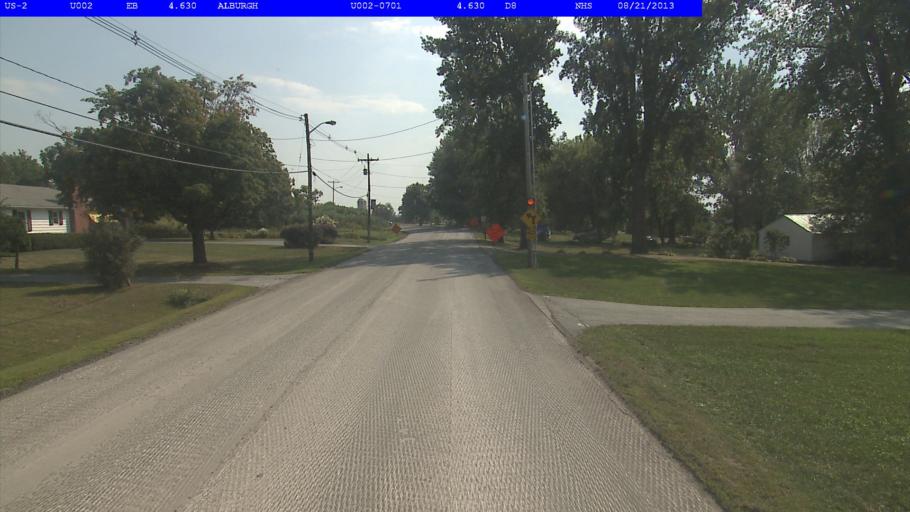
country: US
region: New York
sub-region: Clinton County
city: Rouses Point
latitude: 44.9677
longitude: -73.3030
